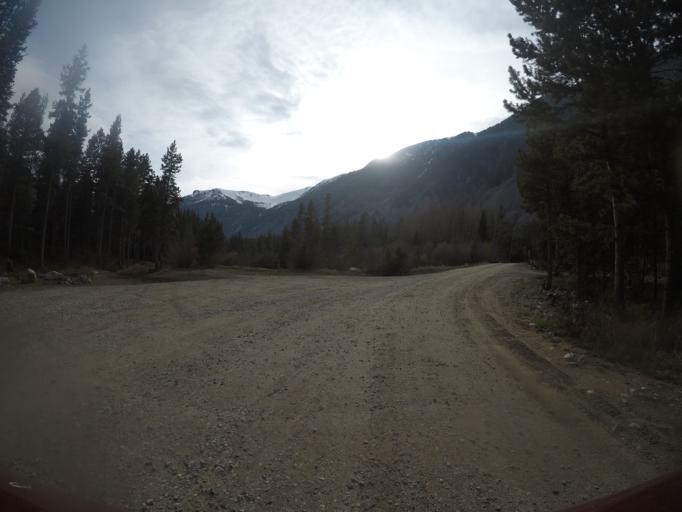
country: US
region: Montana
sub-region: Carbon County
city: Red Lodge
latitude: 45.0277
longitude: -109.4380
